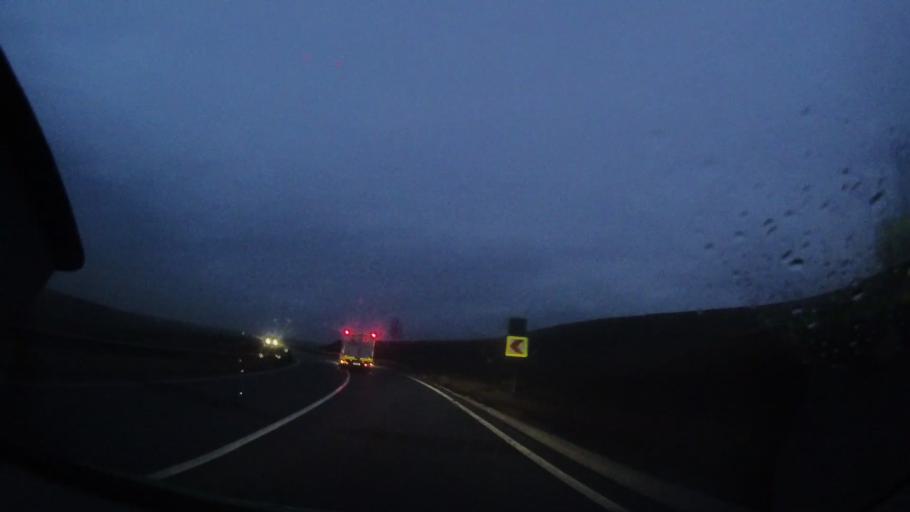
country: RO
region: Harghita
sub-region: Comuna Subcetate
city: Subcetate
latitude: 46.8490
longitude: 25.4687
